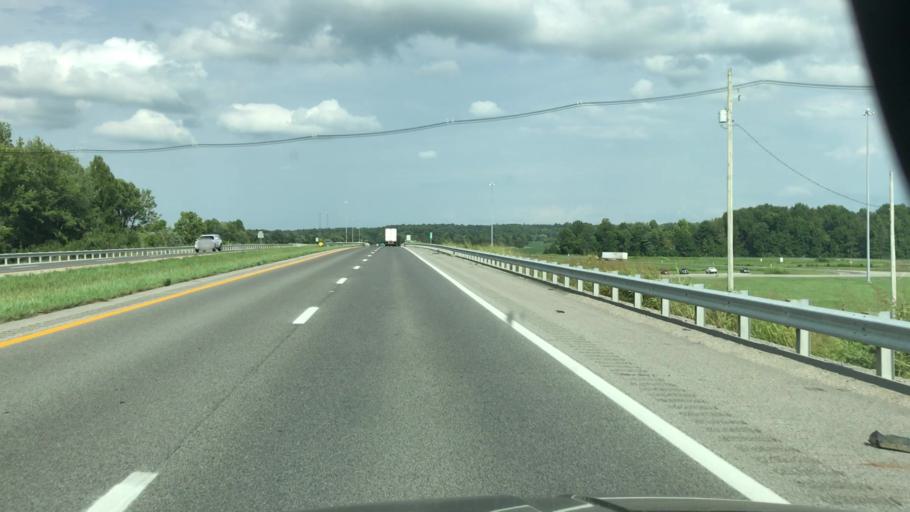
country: US
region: Kentucky
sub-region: Muhlenberg County
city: Greenville
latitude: 37.2338
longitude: -87.2771
